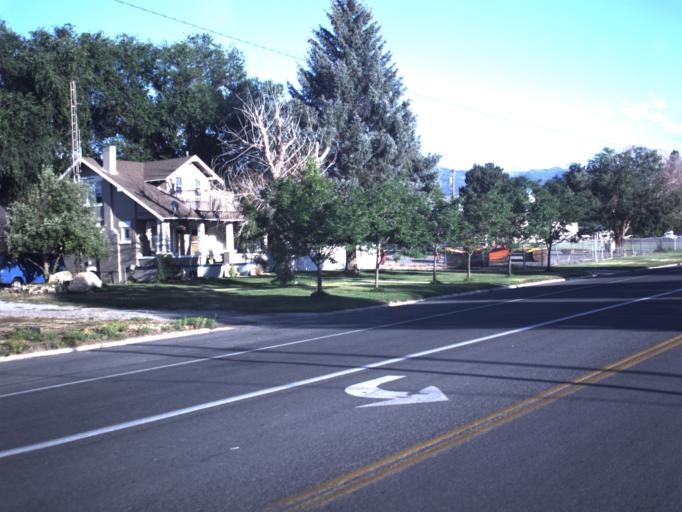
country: US
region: Utah
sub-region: Sanpete County
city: Mount Pleasant
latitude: 39.5542
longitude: -111.4555
